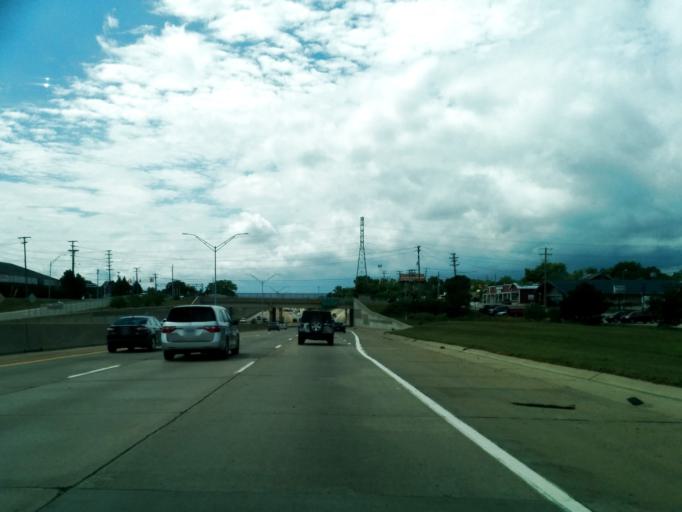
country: US
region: Michigan
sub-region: Macomb County
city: Utica
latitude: 42.6251
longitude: -83.0388
